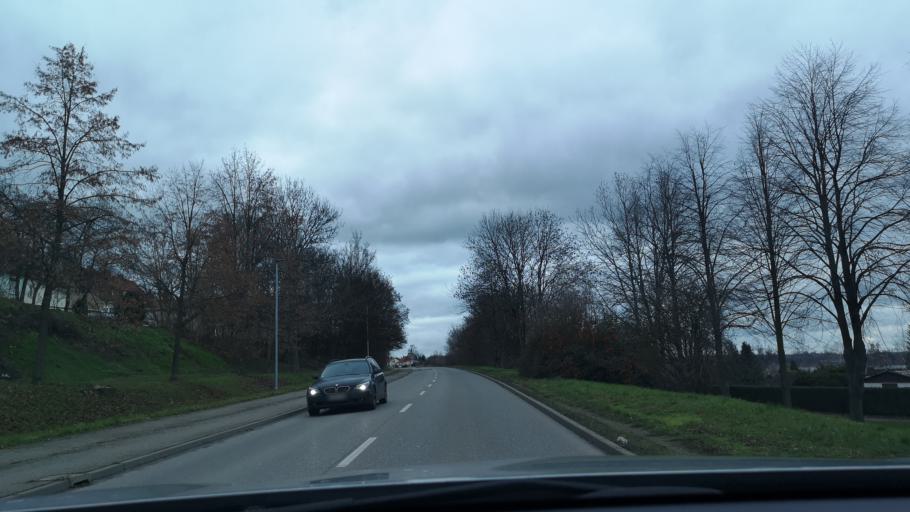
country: DE
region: Saxony-Anhalt
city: Krumpa
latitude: 51.2980
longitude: 11.8426
